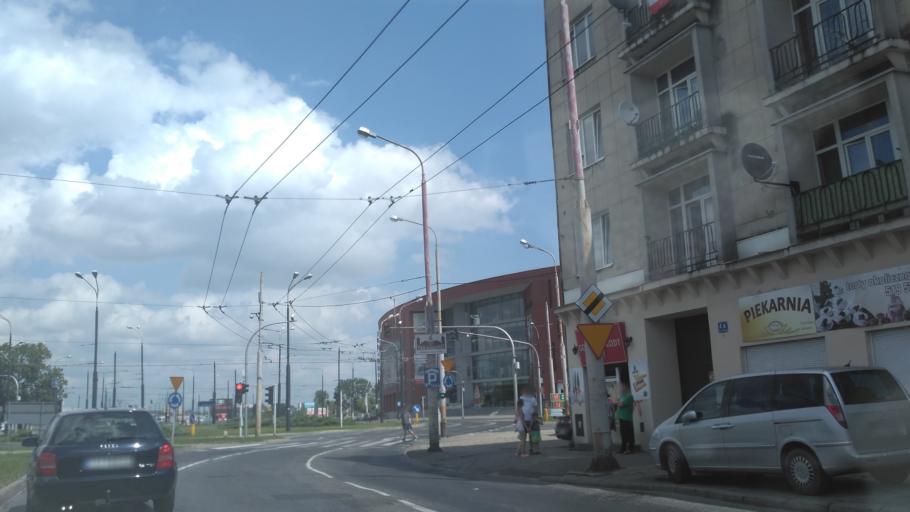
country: PL
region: Lublin Voivodeship
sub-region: Powiat lubelski
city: Lublin
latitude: 51.2375
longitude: 22.5714
